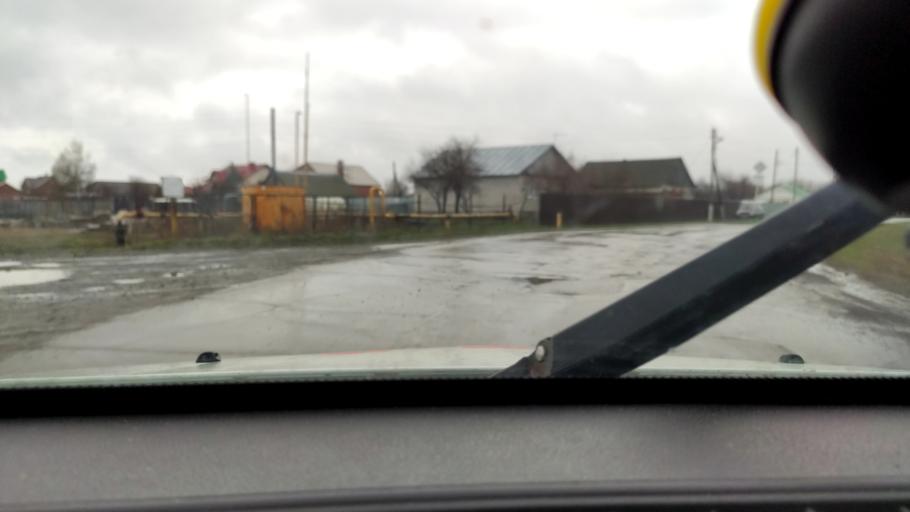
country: RU
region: Samara
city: Povolzhskiy
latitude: 53.6473
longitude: 49.6873
